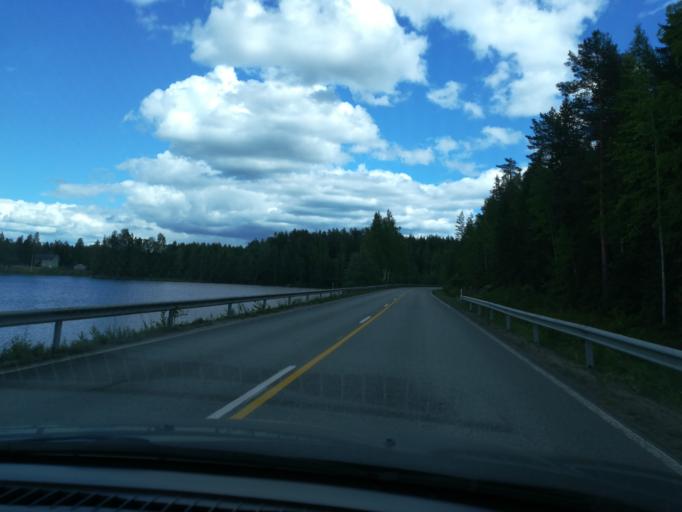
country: FI
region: Southern Savonia
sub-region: Mikkeli
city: Hirvensalmi
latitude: 61.6702
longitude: 26.8724
